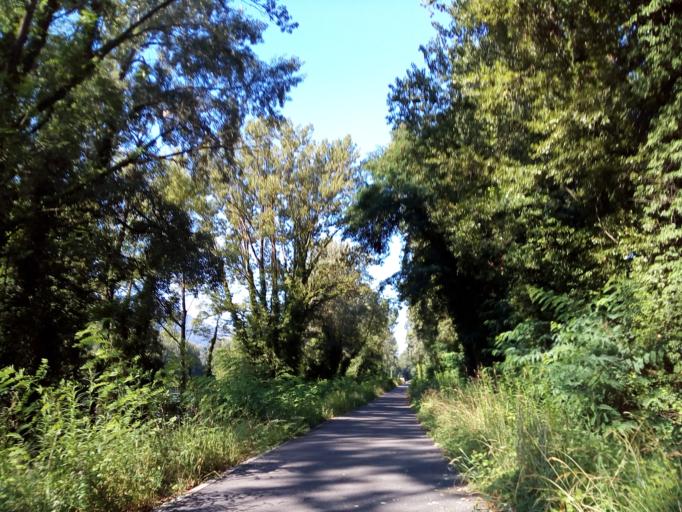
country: FR
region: Rhone-Alpes
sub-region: Departement de l'Isere
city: Le Versoud
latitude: 45.2266
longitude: 5.8486
